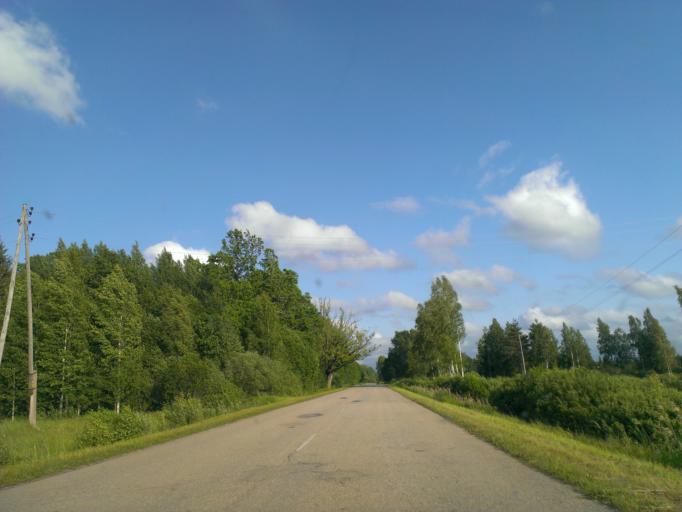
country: LV
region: Aizpute
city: Aizpute
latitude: 56.7924
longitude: 21.5073
